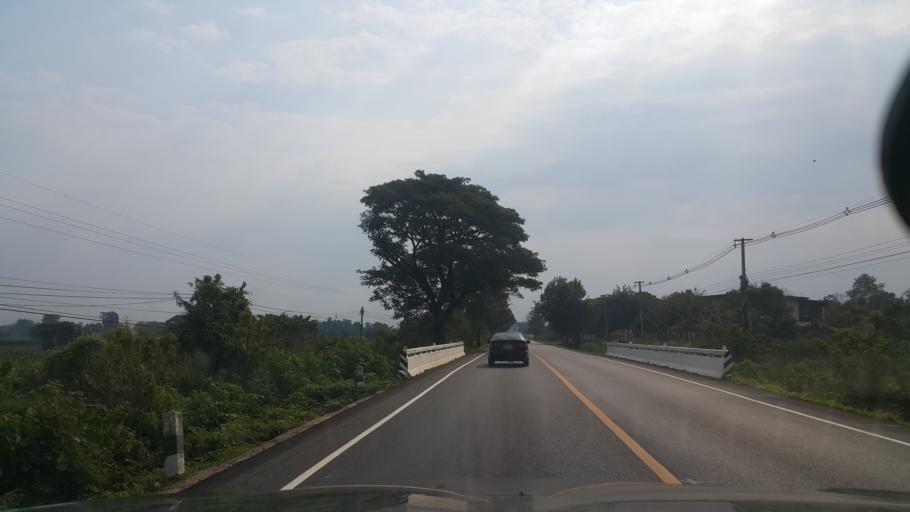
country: TH
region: Sukhothai
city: Si Samrong
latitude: 17.1777
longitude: 99.8458
